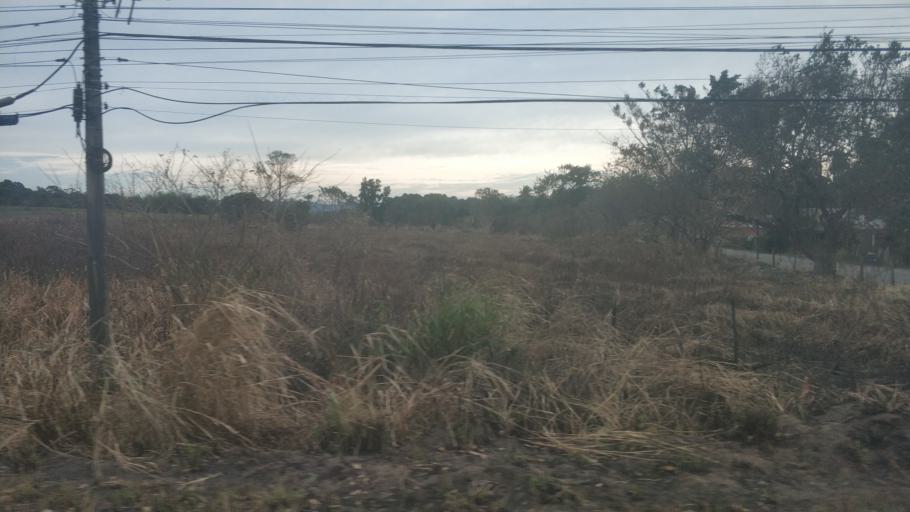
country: BR
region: Rio de Janeiro
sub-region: Seropedica
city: Seropedica
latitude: -22.7709
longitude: -43.6720
